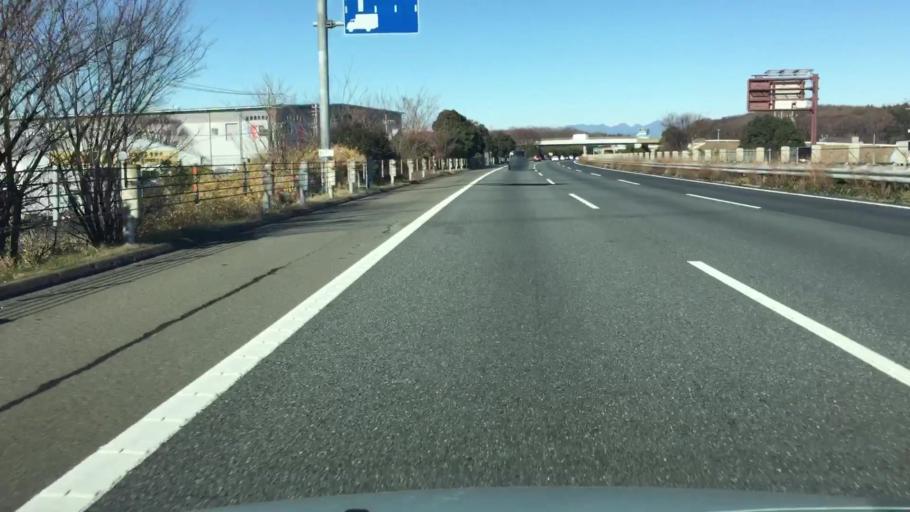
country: JP
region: Saitama
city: Honjo
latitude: 36.2042
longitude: 139.1761
